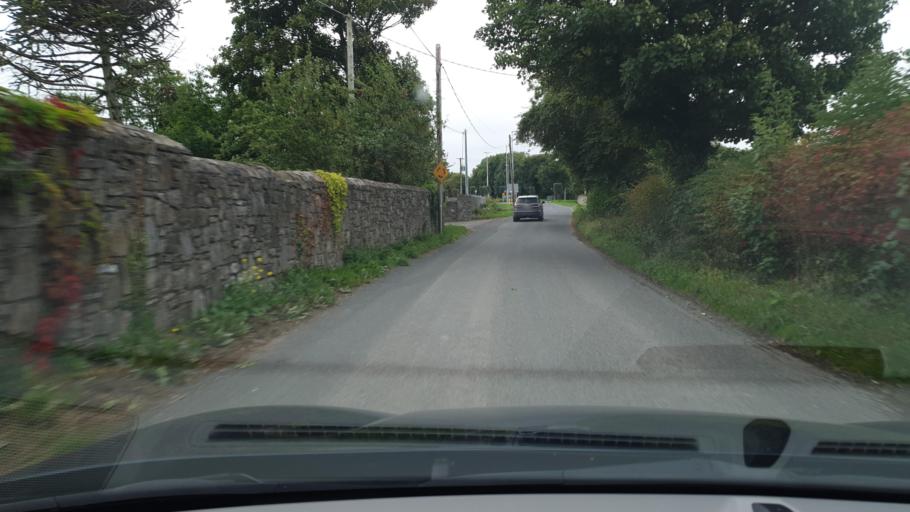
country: IE
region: Leinster
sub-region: An Mhi
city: Ratoath
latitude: 53.5512
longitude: -6.4496
